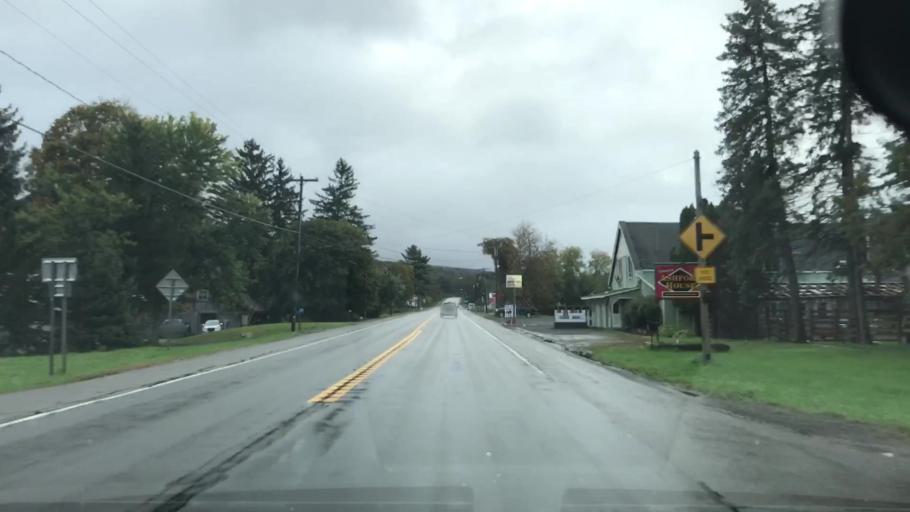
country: US
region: New York
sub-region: Erie County
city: Springville
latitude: 42.4032
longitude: -78.6853
